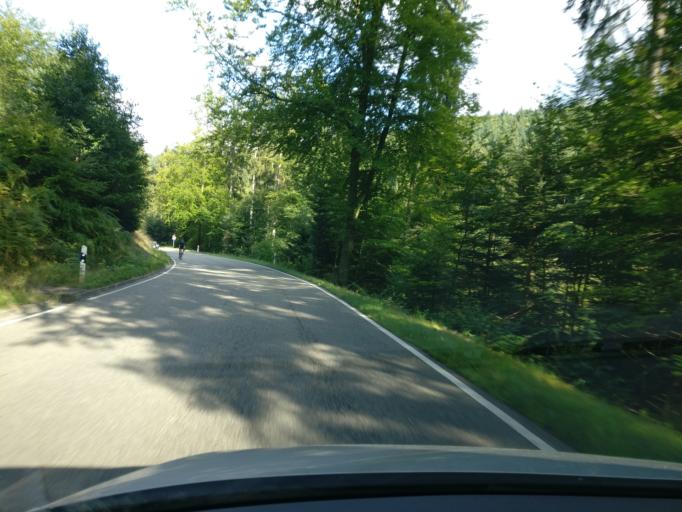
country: DE
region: Baden-Wuerttemberg
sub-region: Karlsruhe Region
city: Loffenau
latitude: 48.7892
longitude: 8.4050
